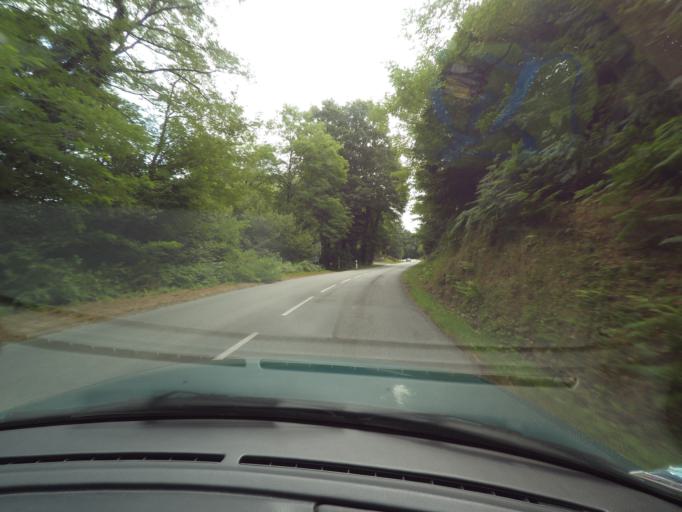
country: FR
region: Limousin
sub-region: Departement de la Haute-Vienne
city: Eymoutiers
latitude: 45.7365
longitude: 1.7567
